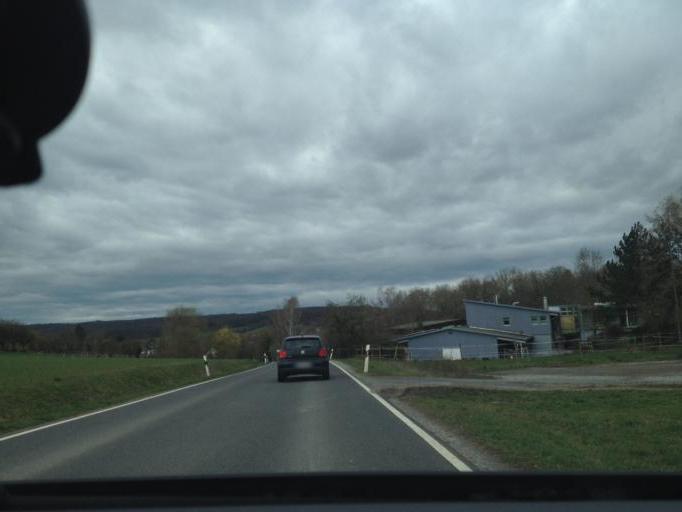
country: DE
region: Bavaria
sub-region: Regierungsbezirk Unterfranken
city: Reichenberg
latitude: 49.7314
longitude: 9.9239
